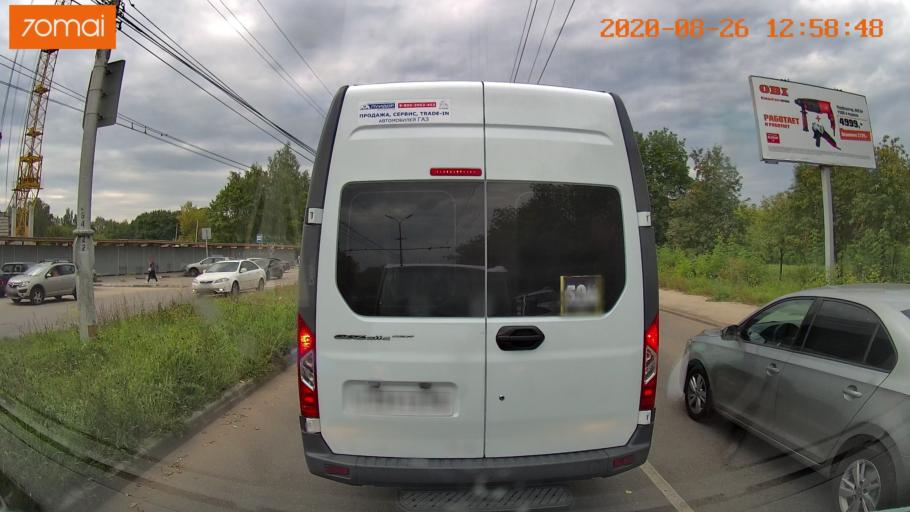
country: RU
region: Rjazan
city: Ryazan'
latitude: 54.6143
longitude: 39.7453
